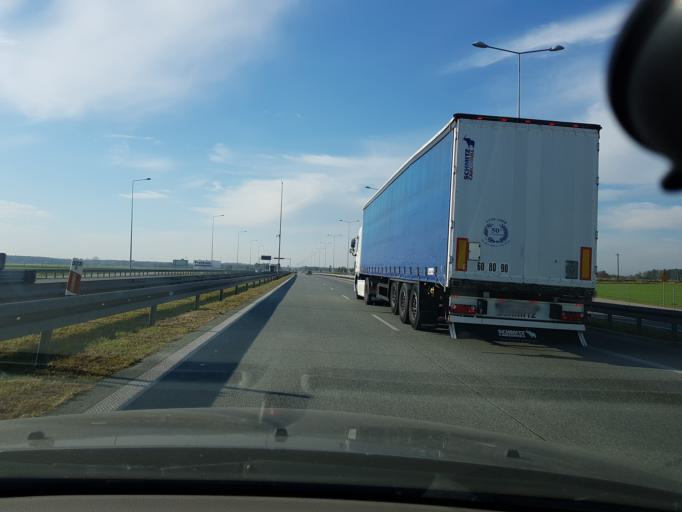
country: PL
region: Lodz Voivodeship
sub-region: Powiat tomaszowski
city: Czerniewice
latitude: 51.6753
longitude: 20.1847
